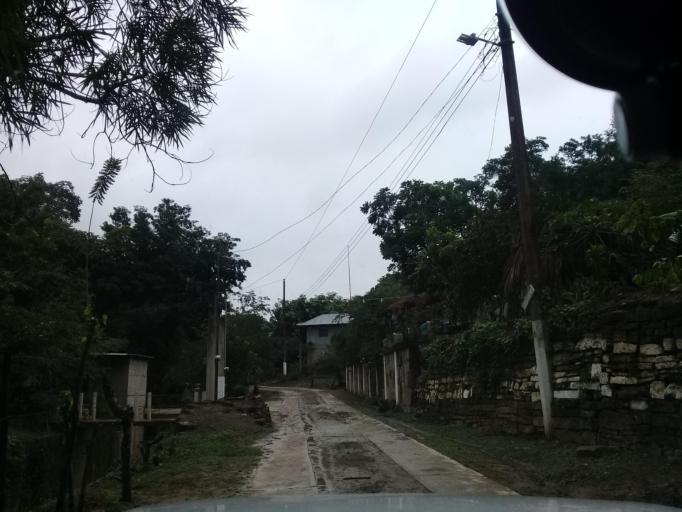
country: MX
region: Veracruz
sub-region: Chalma
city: San Pedro Coyutla
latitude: 21.2436
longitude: -98.4241
